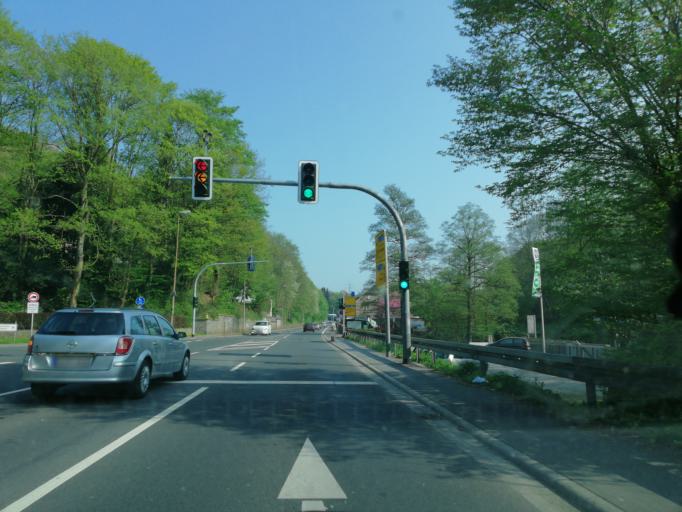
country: DE
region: North Rhine-Westphalia
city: Herdecke
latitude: 51.4124
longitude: 7.4314
